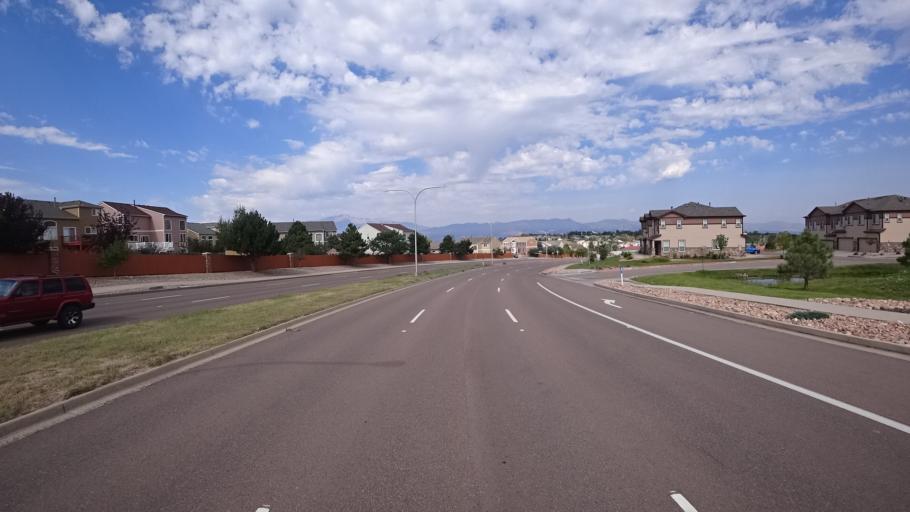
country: US
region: Colorado
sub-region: El Paso County
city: Cimarron Hills
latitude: 38.9110
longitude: -104.7299
